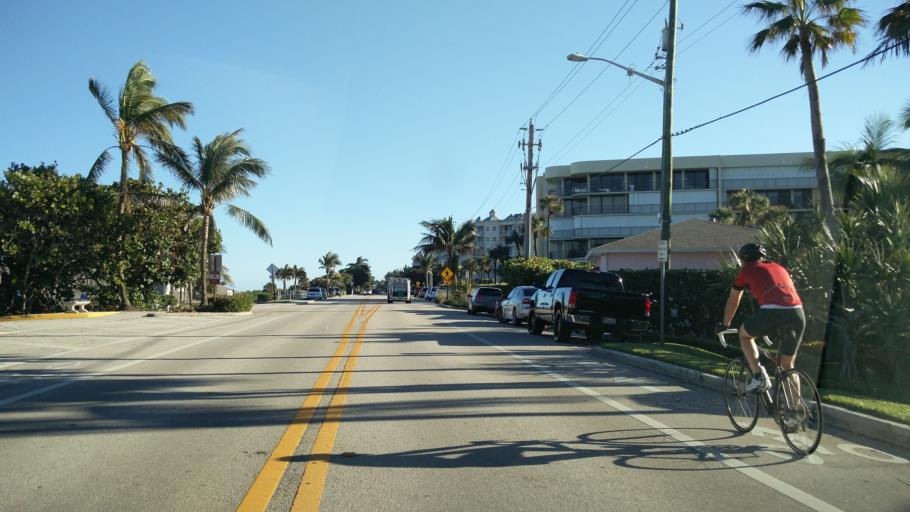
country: US
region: Florida
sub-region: Palm Beach County
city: Jupiter
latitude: 26.9220
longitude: -80.0667
